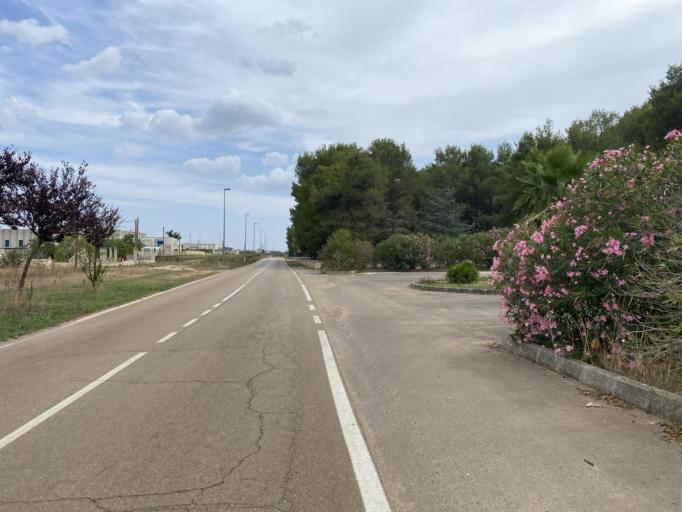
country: IT
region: Apulia
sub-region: Provincia di Lecce
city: Giuggianello
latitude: 40.0872
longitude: 18.3707
